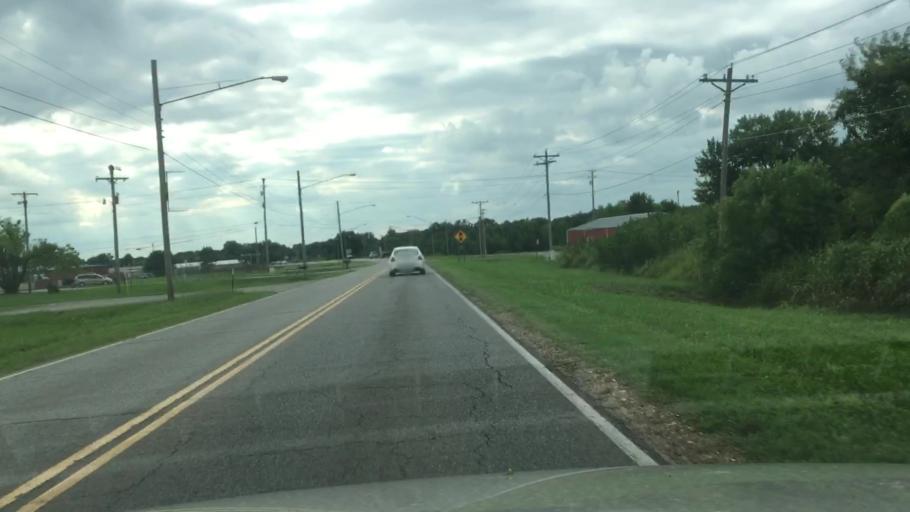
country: US
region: Oklahoma
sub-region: Cherokee County
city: Tahlequah
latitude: 35.9195
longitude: -94.9985
